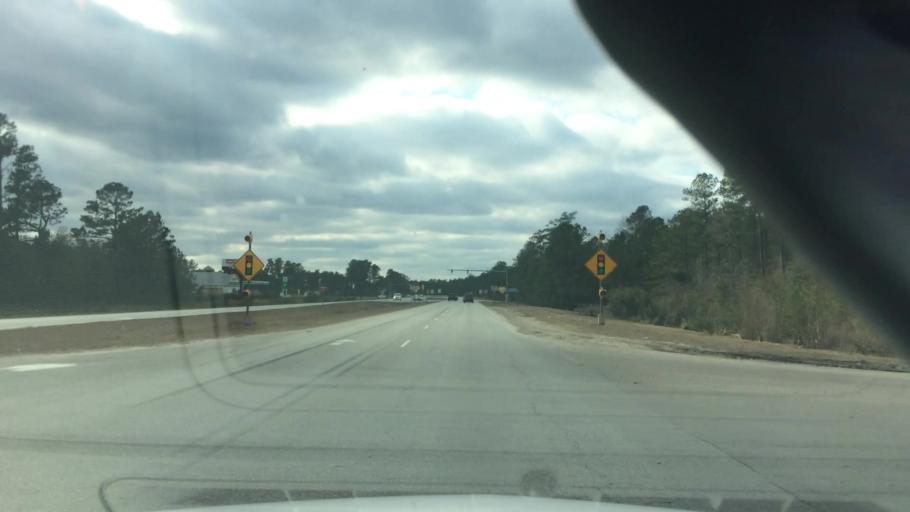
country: US
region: North Carolina
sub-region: Brunswick County
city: Bolivia
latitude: 34.0402
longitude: -78.2448
